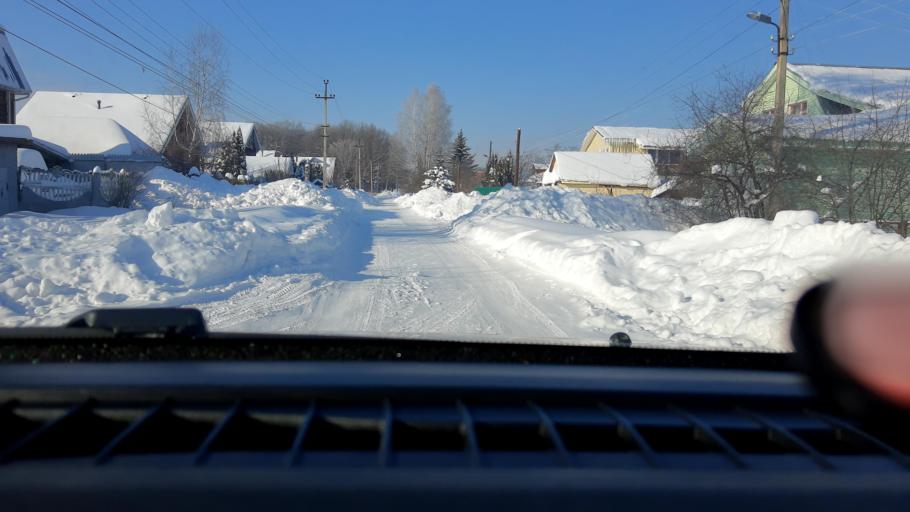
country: RU
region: Nizjnij Novgorod
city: Afonino
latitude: 56.1985
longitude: 44.0374
